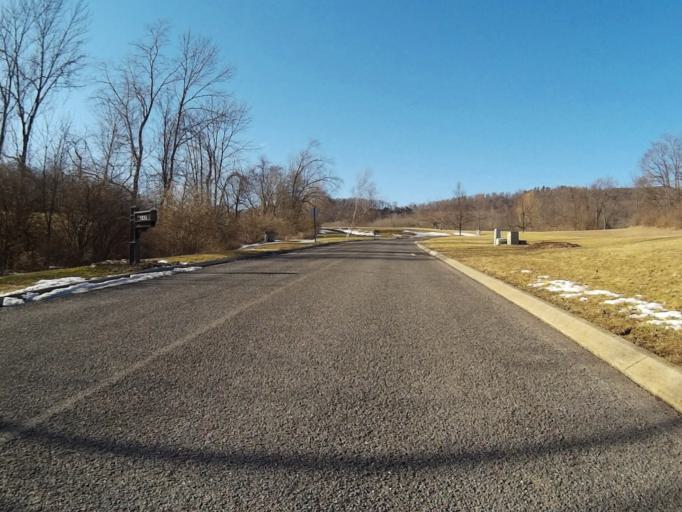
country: US
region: Pennsylvania
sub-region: Centre County
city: Park Forest Village
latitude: 40.8405
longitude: -77.9250
